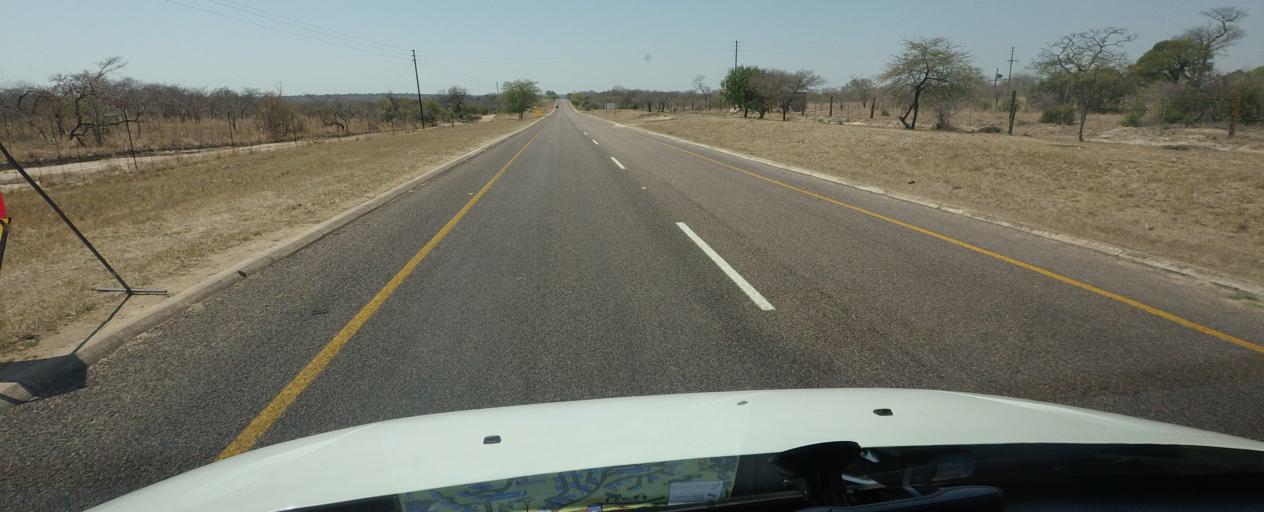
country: ZA
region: Limpopo
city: Thulamahashi
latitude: -24.5611
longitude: 31.1612
